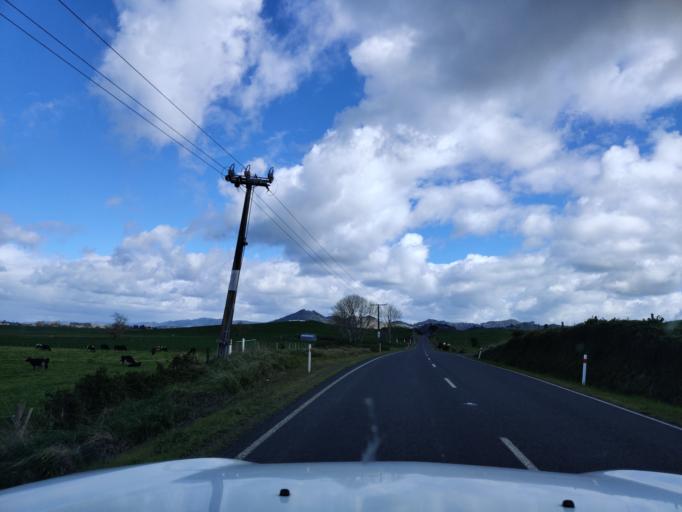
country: NZ
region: Waikato
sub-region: Waikato District
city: Ngaruawahia
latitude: -37.5752
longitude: 175.2397
